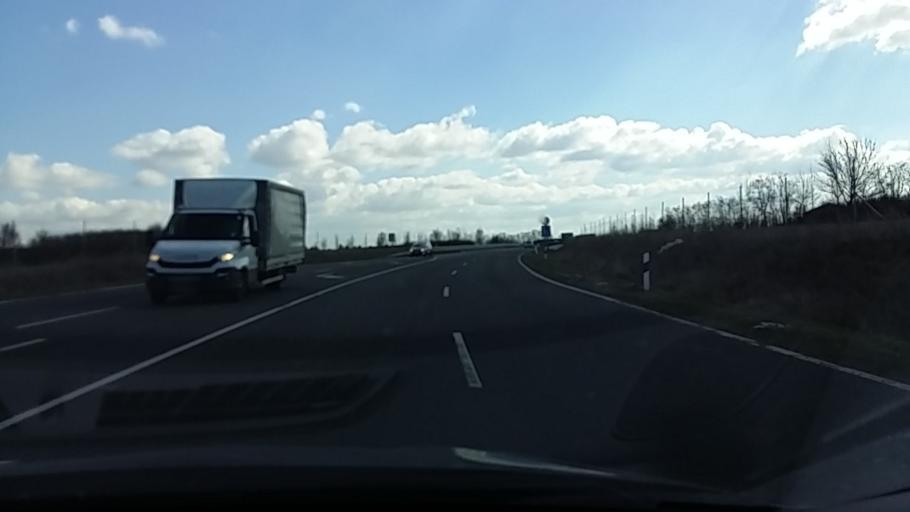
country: HU
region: Baranya
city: Kozarmisleny
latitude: 46.0210
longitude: 18.2867
